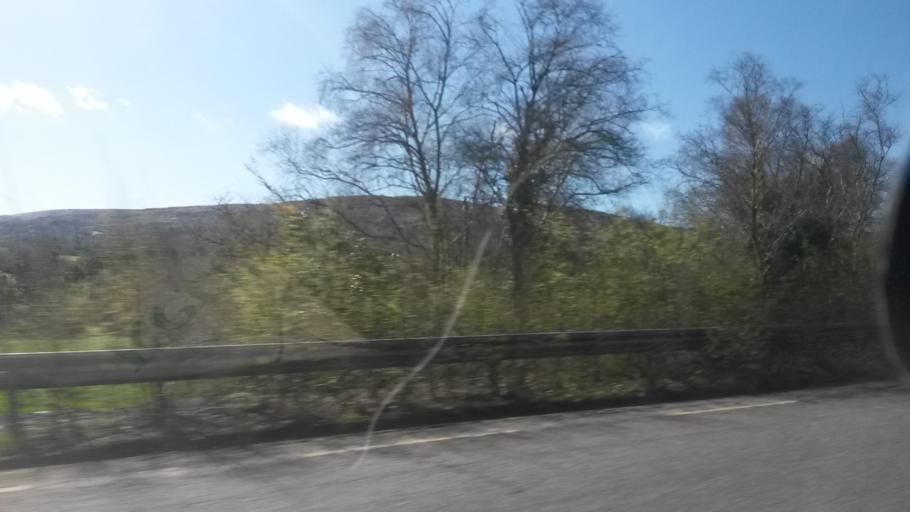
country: IE
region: Munster
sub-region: Ciarrai
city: Cill Airne
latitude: 51.9171
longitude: -9.3914
